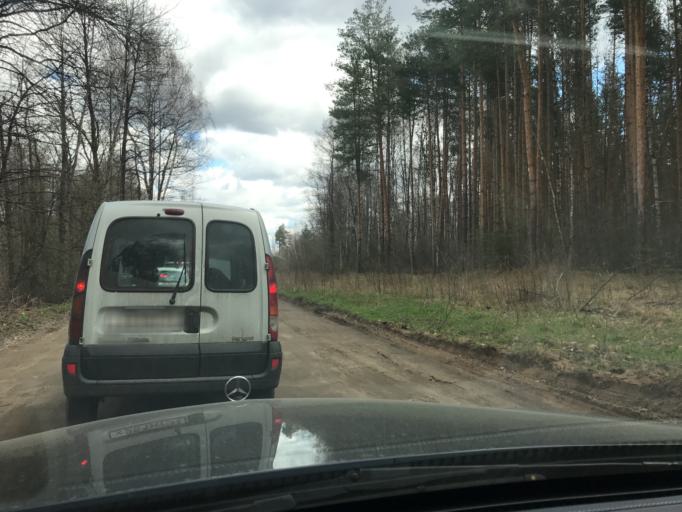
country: RU
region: Vladimir
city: Pokrov
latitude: 55.8775
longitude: 39.2471
